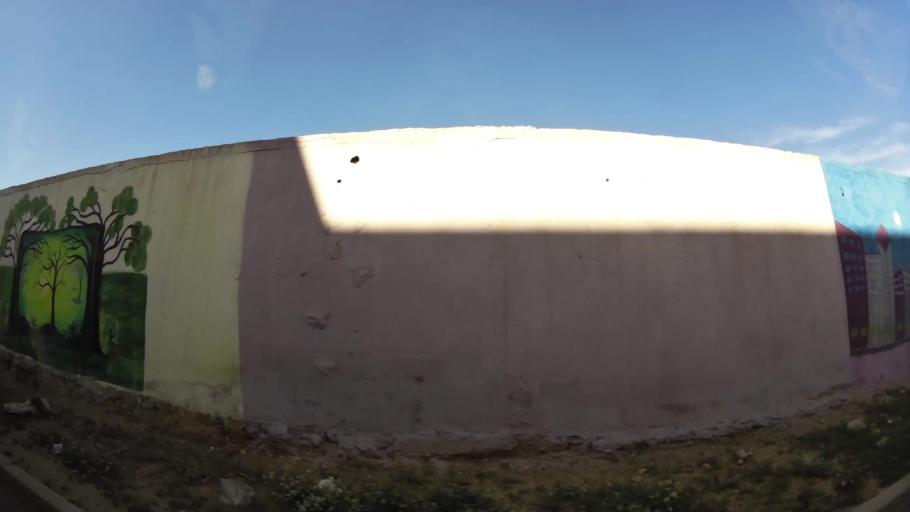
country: MA
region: Oriental
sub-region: Oujda-Angad
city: Oujda
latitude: 34.6590
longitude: -1.9495
